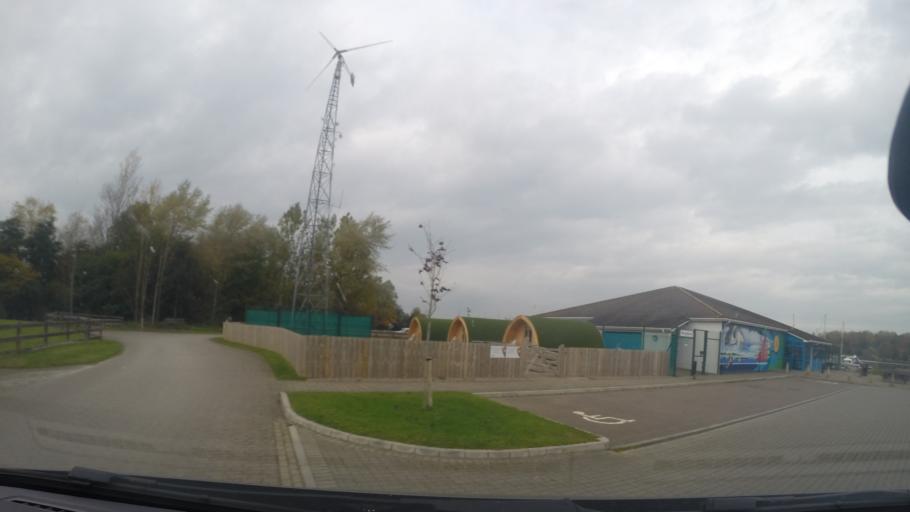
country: GB
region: Northern Ireland
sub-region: Craigavon District
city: Craigavon
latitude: 54.4890
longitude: -6.3663
